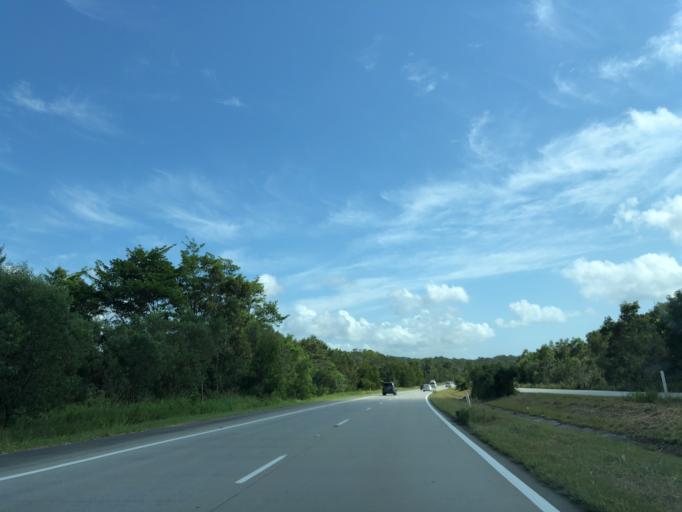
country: AU
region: New South Wales
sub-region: Byron Shire
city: Brunswick Heads
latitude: -28.5715
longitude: 153.5408
